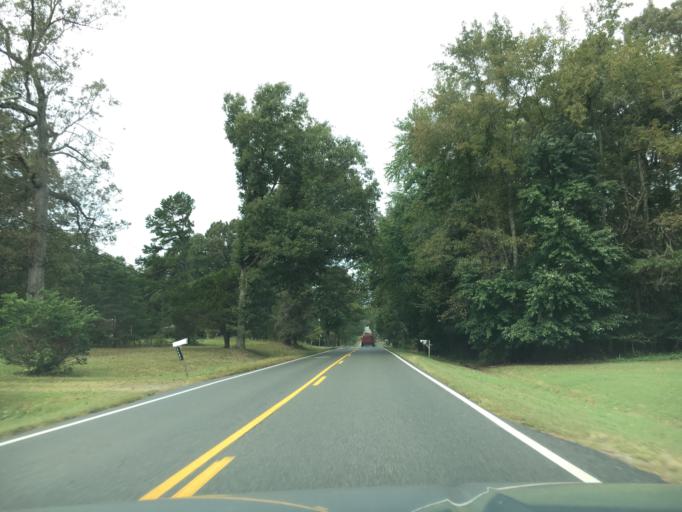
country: US
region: Virginia
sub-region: Goochland County
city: Goochland
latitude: 37.7540
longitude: -77.8648
